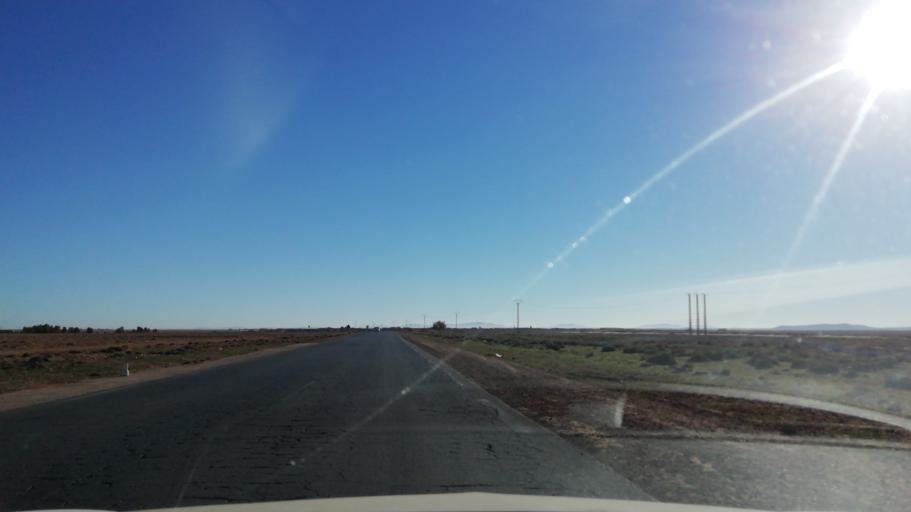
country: DZ
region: El Bayadh
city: El Bayadh
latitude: 33.8543
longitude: 0.6079
